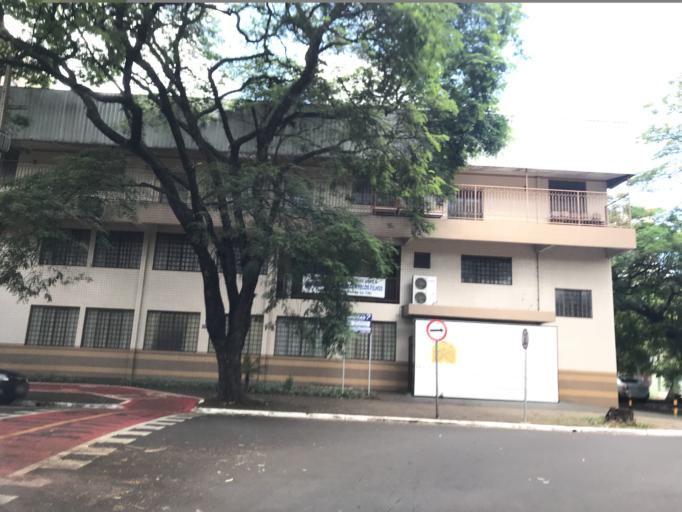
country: BR
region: Parana
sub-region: Maringa
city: Maringa
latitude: -23.4155
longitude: -51.9262
